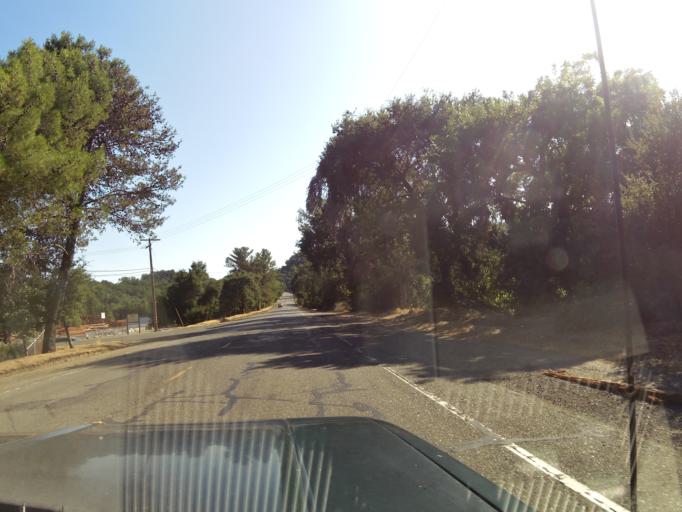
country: US
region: California
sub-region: Sonoma County
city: Cloverdale
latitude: 38.8237
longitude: -123.0182
